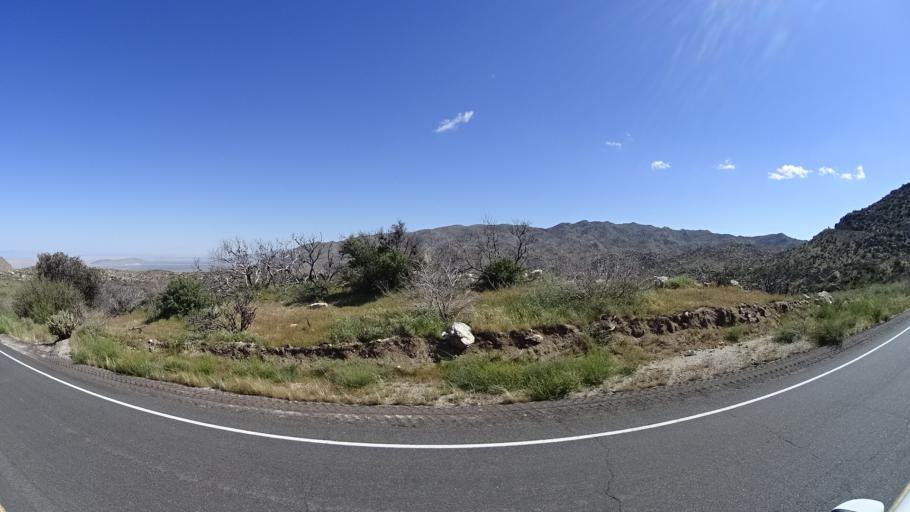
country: US
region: California
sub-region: San Diego County
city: Borrego Springs
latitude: 33.2196
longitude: -116.4629
